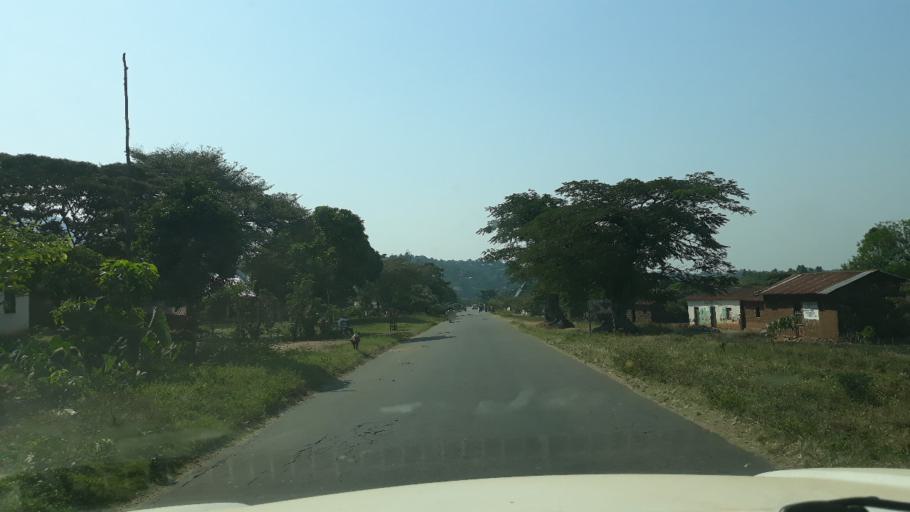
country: CD
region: South Kivu
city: Uvira
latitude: -3.2474
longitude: 29.1612
